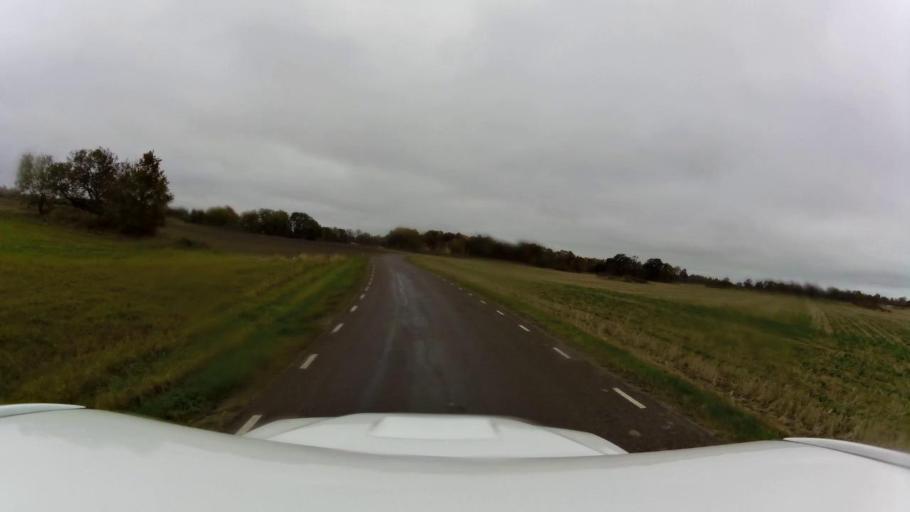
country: SE
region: OEstergoetland
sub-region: Linkopings Kommun
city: Linghem
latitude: 58.4816
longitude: 15.7312
